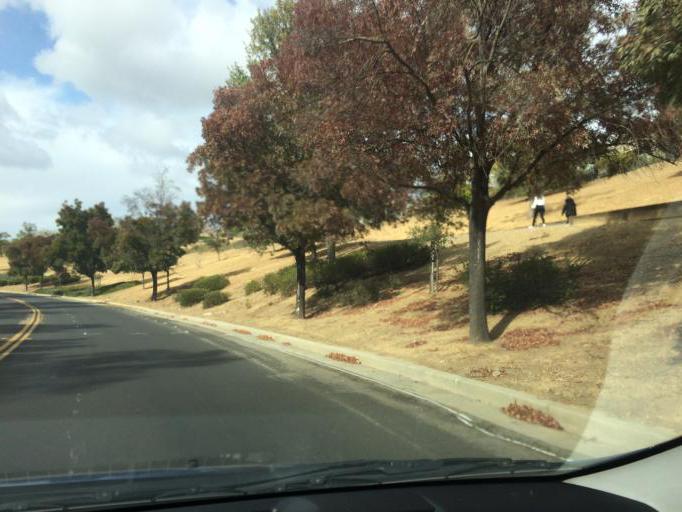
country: US
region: California
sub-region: Santa Clara County
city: Seven Trees
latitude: 37.2832
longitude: -121.7647
